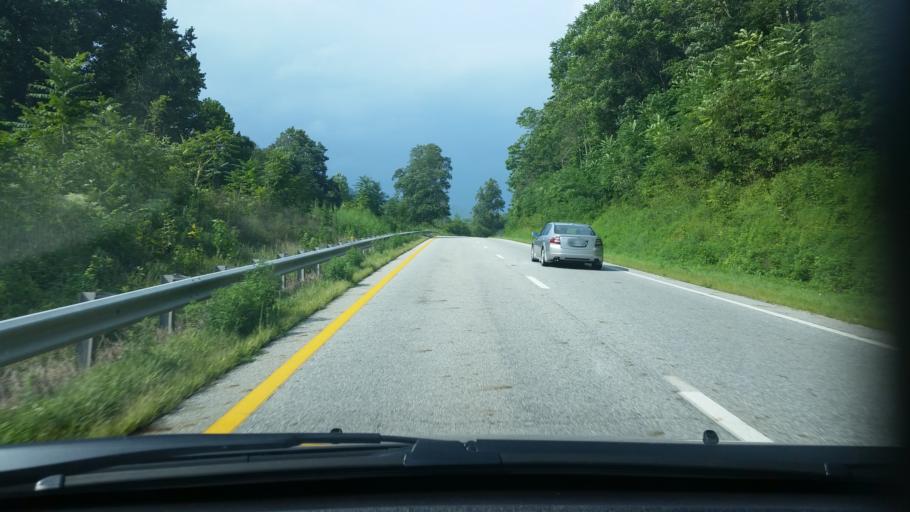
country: US
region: Virginia
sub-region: Nelson County
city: Lovingston
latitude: 37.7907
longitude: -78.8652
